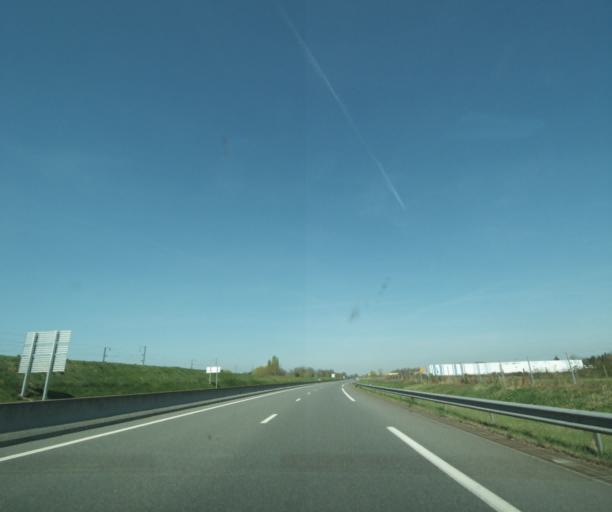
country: FR
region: Auvergne
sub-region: Departement de l'Allier
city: Avermes
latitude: 46.6050
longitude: 3.2983
